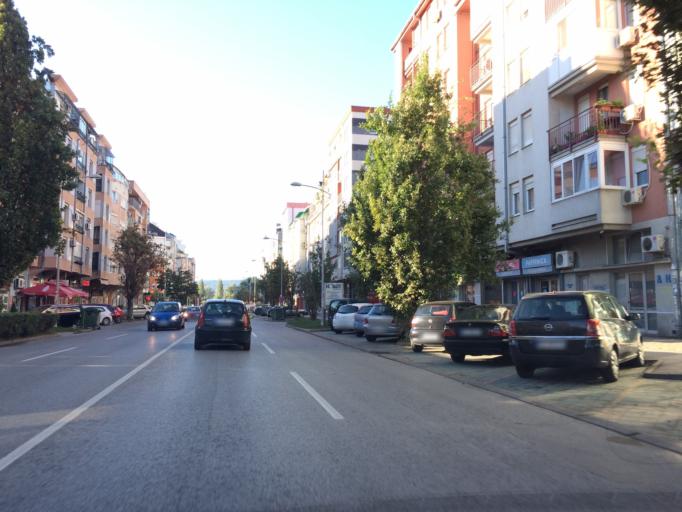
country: RS
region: Autonomna Pokrajina Vojvodina
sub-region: Juznobacki Okrug
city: Novi Sad
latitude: 45.2429
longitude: 19.8252
